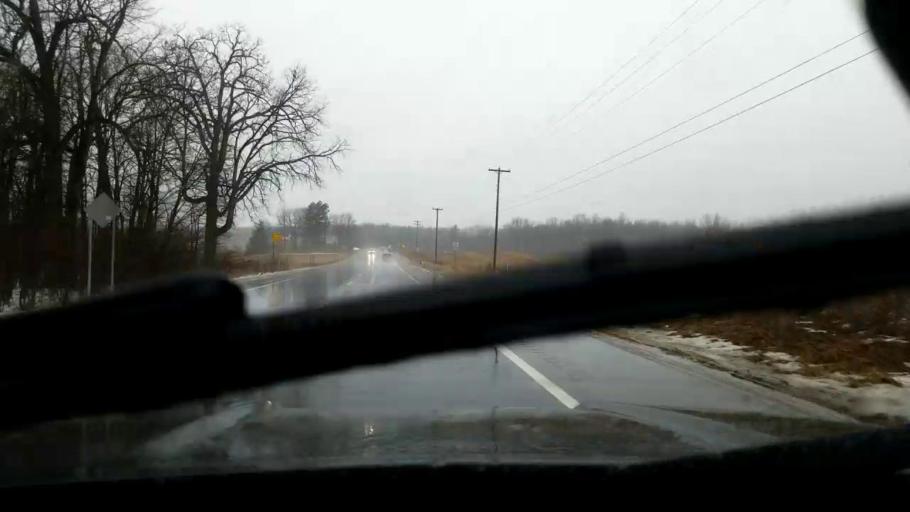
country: US
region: Michigan
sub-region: Jackson County
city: Napoleon
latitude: 42.1794
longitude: -84.2887
